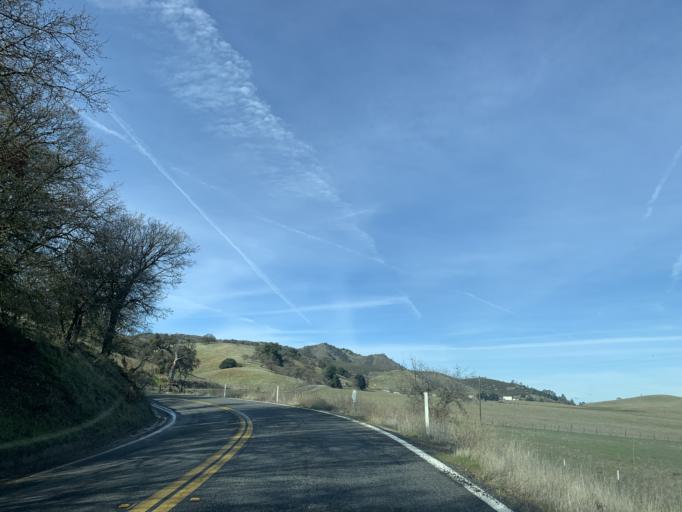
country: US
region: California
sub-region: Monterey County
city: Soledad
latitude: 36.5624
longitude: -121.1774
